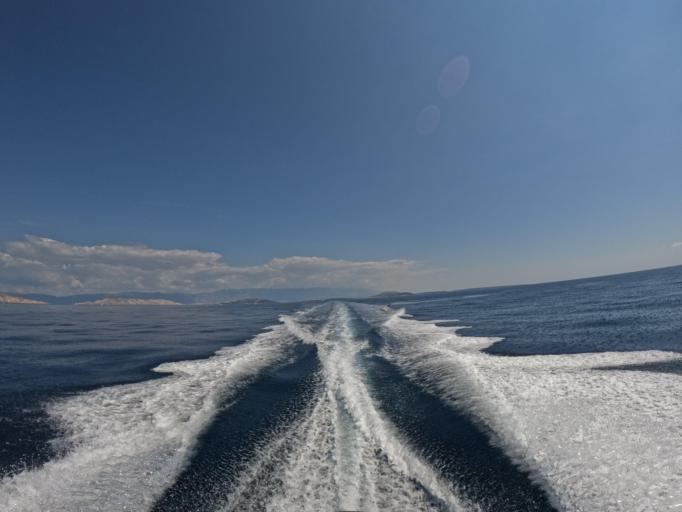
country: HR
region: Primorsko-Goranska
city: Punat
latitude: 44.9065
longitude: 14.6002
